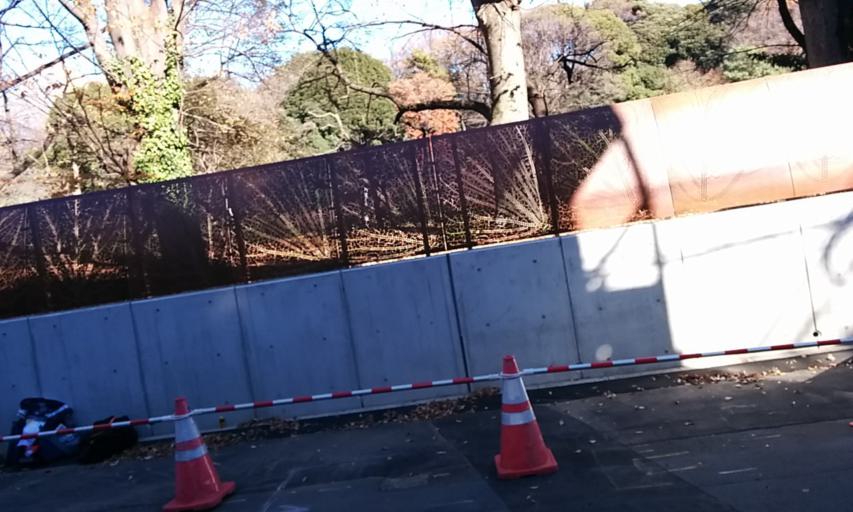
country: JP
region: Tokyo
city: Tokyo
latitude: 35.7207
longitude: 139.7414
